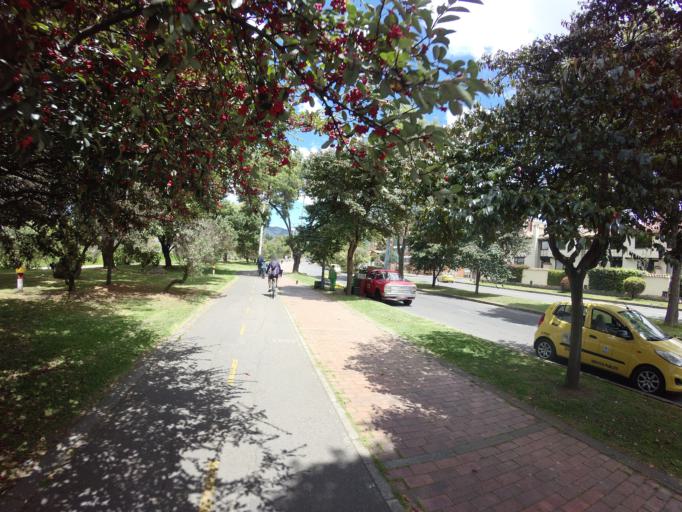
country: CO
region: Bogota D.C.
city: Barrio San Luis
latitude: 4.6975
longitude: -74.0638
